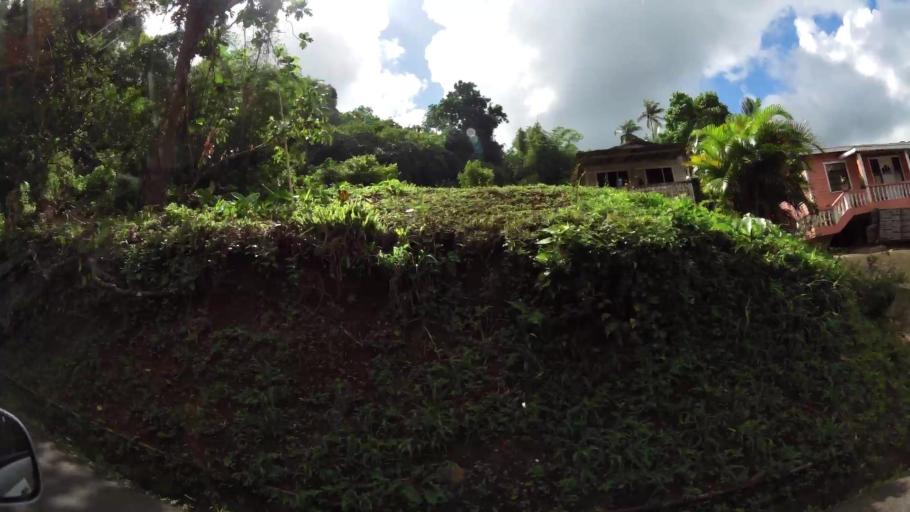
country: GD
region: Saint Andrew
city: Grenville
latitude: 12.1131
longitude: -61.6731
